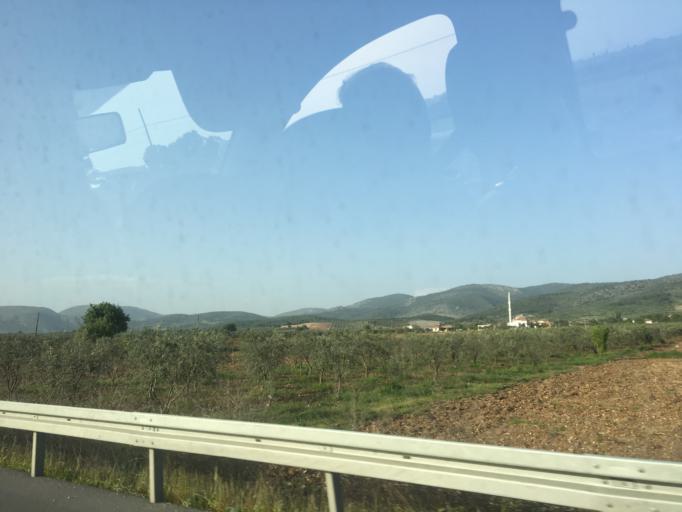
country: TR
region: Manisa
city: Golmarmara
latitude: 38.7907
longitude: 27.9010
